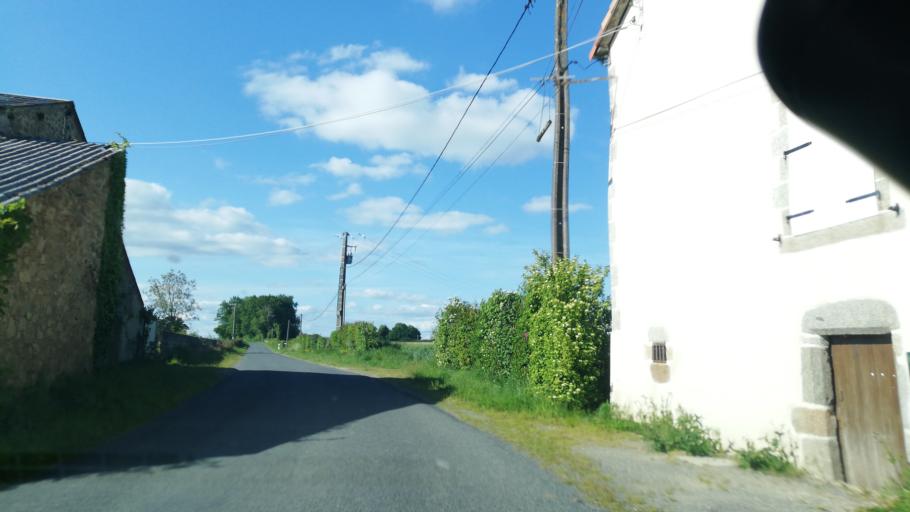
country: FR
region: Poitou-Charentes
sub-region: Departement des Deux-Sevres
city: Moncoutant
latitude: 46.6874
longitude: -0.5723
